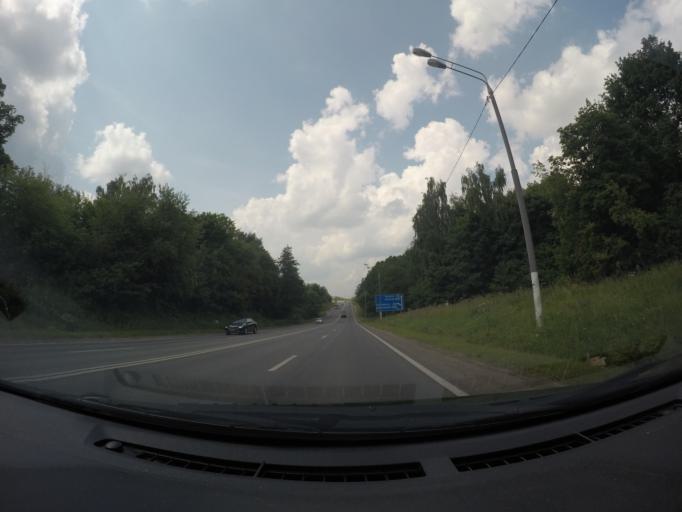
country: RU
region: Moskovskaya
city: Ramenskoye
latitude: 55.4812
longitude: 38.1757
